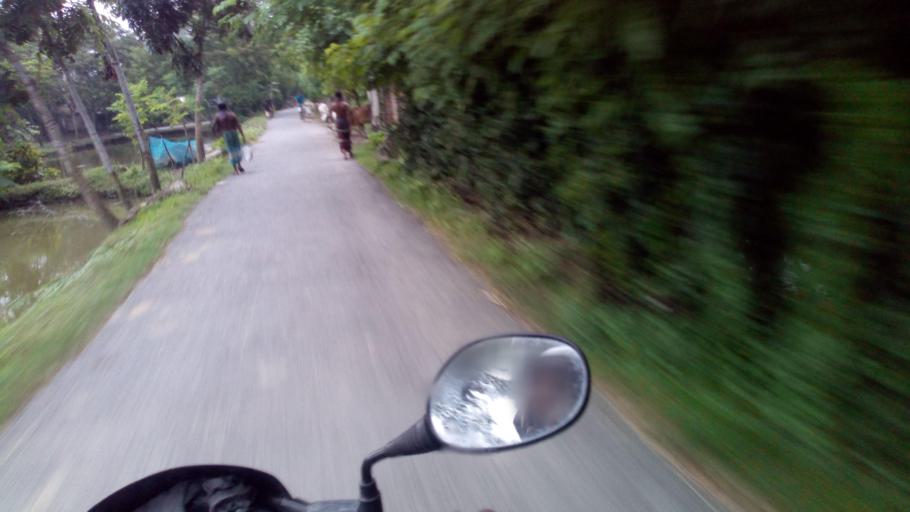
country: BD
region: Khulna
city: Phultala
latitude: 22.7716
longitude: 89.4081
